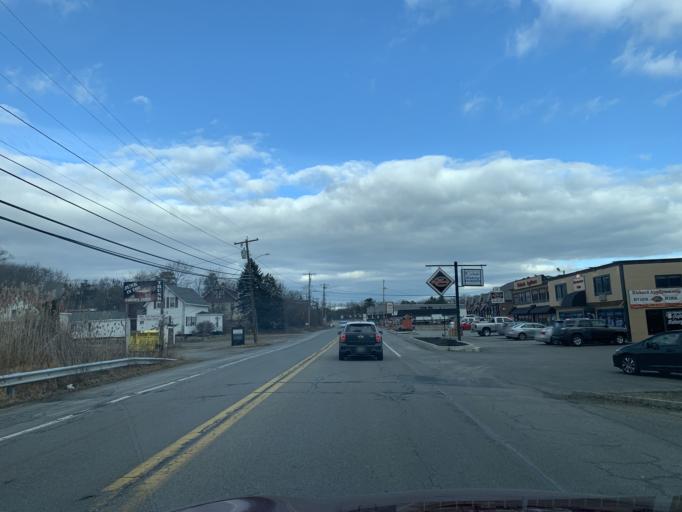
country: US
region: Massachusetts
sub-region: Essex County
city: Newburyport
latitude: 42.8200
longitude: -70.8683
